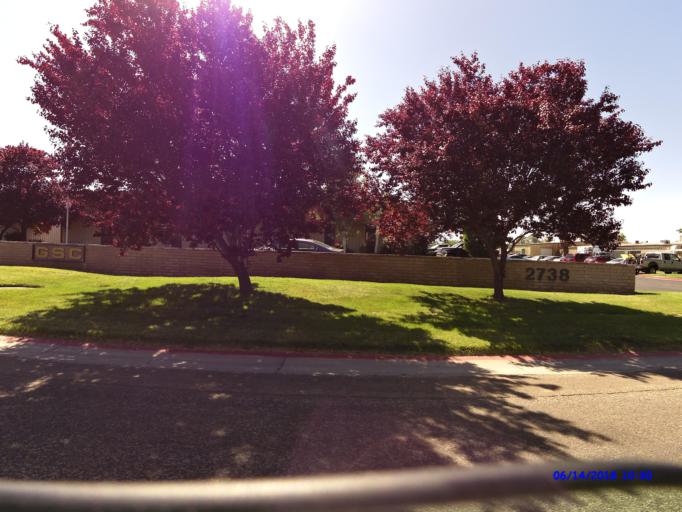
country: US
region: Utah
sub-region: Weber County
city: West Haven
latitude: 41.2158
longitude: -112.0183
